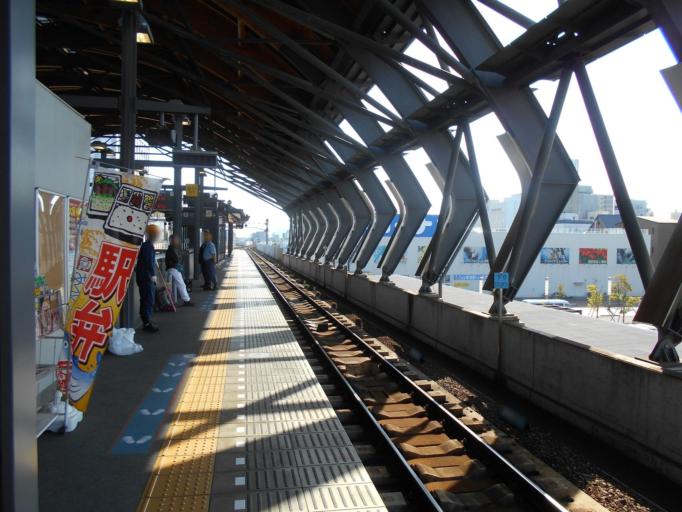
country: JP
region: Kochi
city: Kochi-shi
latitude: 33.5672
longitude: 133.5435
